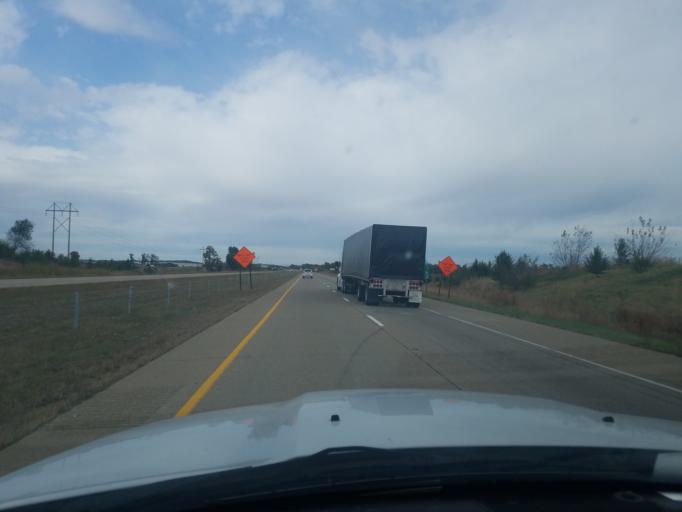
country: US
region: Indiana
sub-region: Vanderburgh County
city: Melody Hill
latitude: 38.0984
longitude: -87.4763
